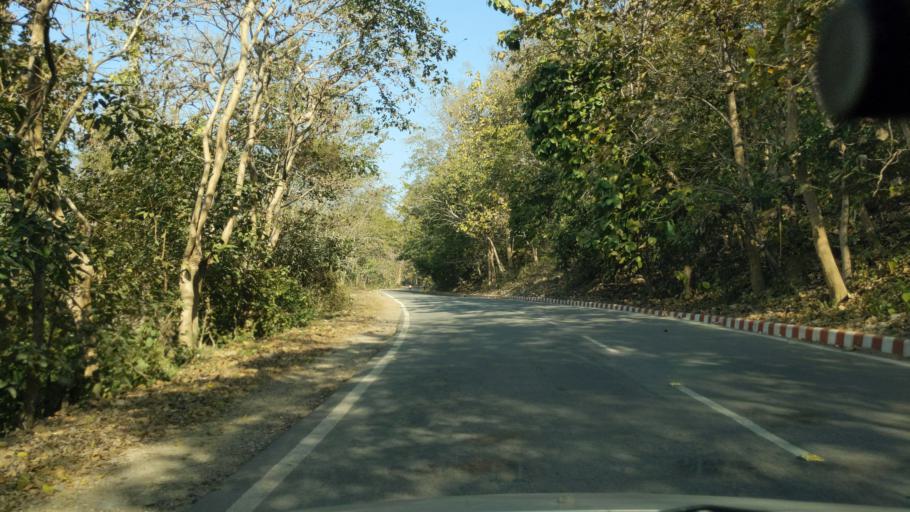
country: IN
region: Uttarakhand
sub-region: Naini Tal
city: Ramnagar
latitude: 29.3941
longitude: 79.1377
